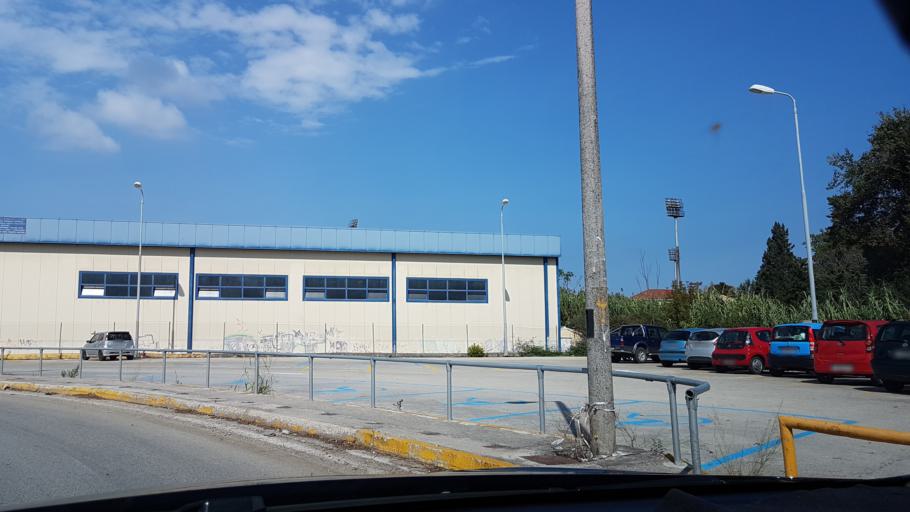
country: GR
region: Ionian Islands
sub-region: Nomos Kerkyras
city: Kerkyra
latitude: 39.6090
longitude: 19.9154
